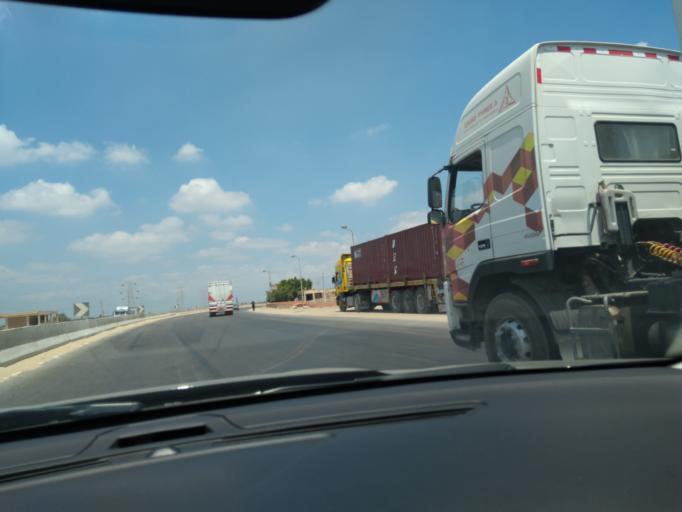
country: EG
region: Muhafazat Bur Sa`id
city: Port Said
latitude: 30.9497
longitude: 32.3080
